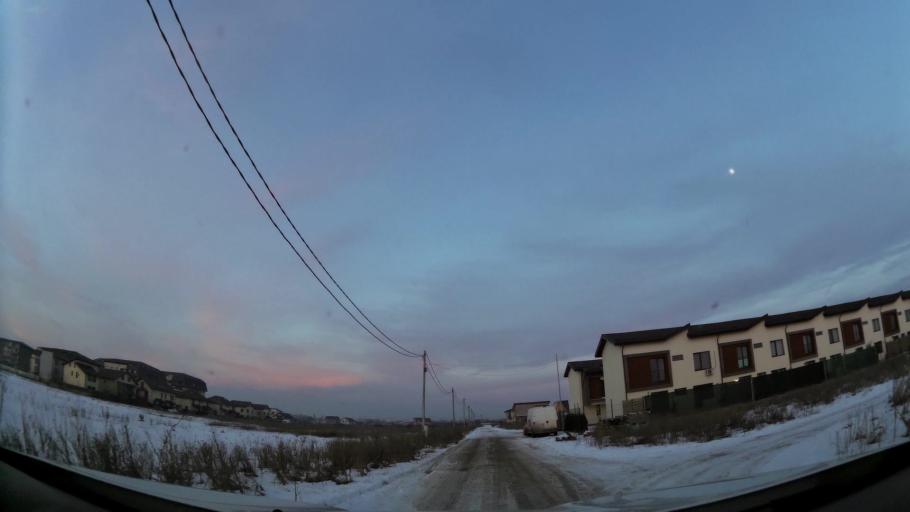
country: RO
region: Ilfov
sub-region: Comuna Magurele
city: Magurele
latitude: 44.3851
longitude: 26.0261
